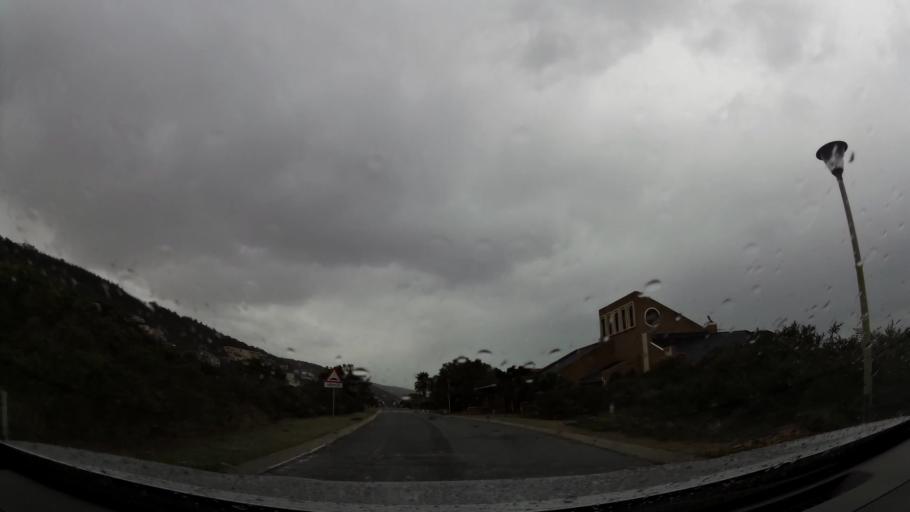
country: ZA
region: Western Cape
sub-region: Eden District Municipality
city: Mossel Bay
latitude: -34.0486
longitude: 22.2859
